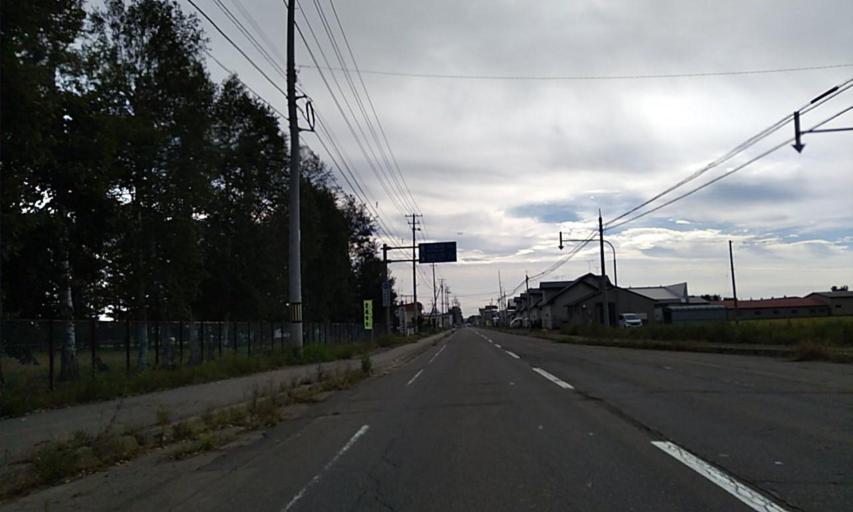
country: JP
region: Hokkaido
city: Obihiro
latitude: 42.8509
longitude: 143.1622
